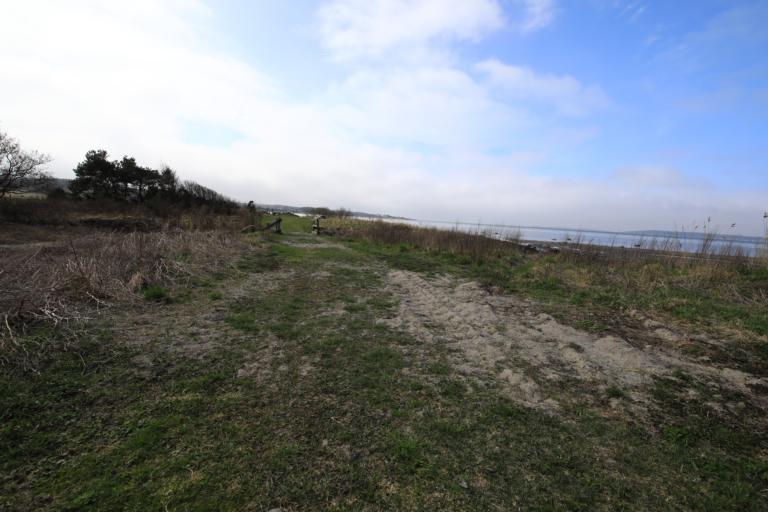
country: SE
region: Halland
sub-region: Kungsbacka Kommun
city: Frillesas
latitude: 57.2867
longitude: 12.1651
